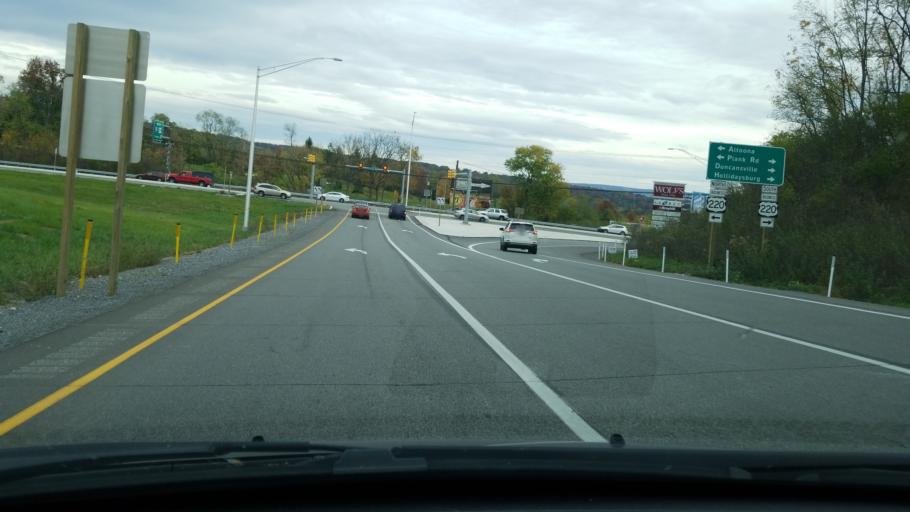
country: US
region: Pennsylvania
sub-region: Blair County
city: Lakemont
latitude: 40.4635
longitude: -78.4097
